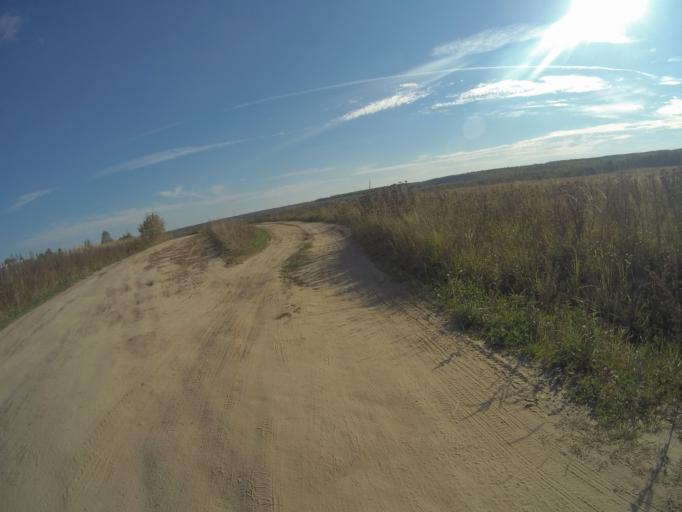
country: RU
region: Vladimir
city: Golovino
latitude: 55.9819
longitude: 40.4477
